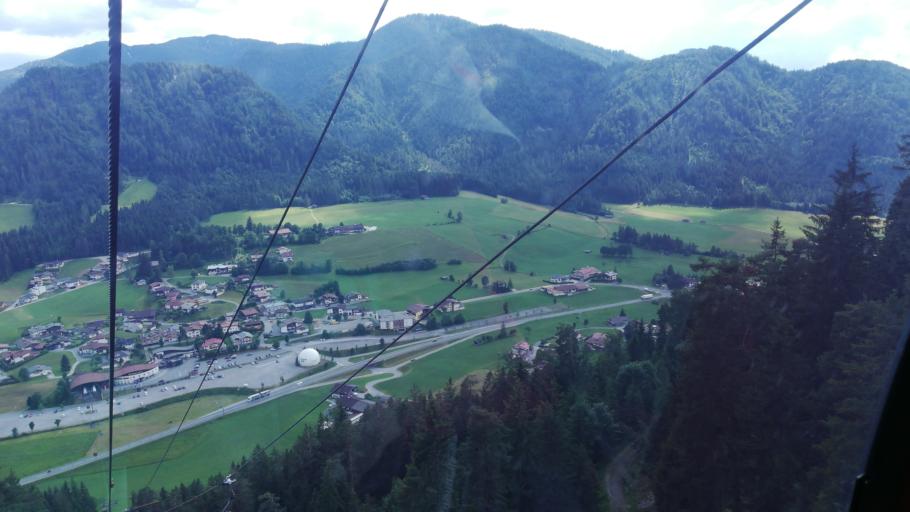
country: AT
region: Tyrol
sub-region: Politischer Bezirk Kitzbuhel
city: Waidring
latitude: 47.5931
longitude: 12.5664
